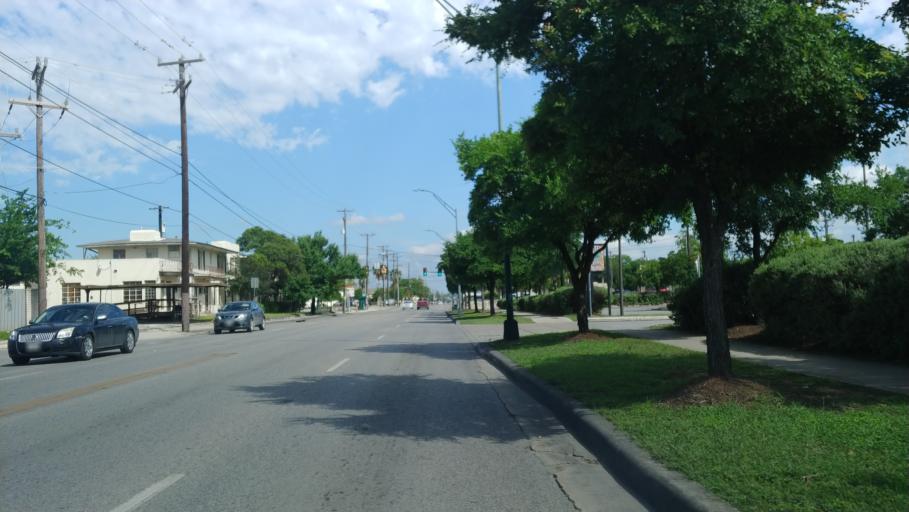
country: US
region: Texas
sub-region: Bexar County
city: Balcones Heights
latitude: 29.4651
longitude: -98.5266
